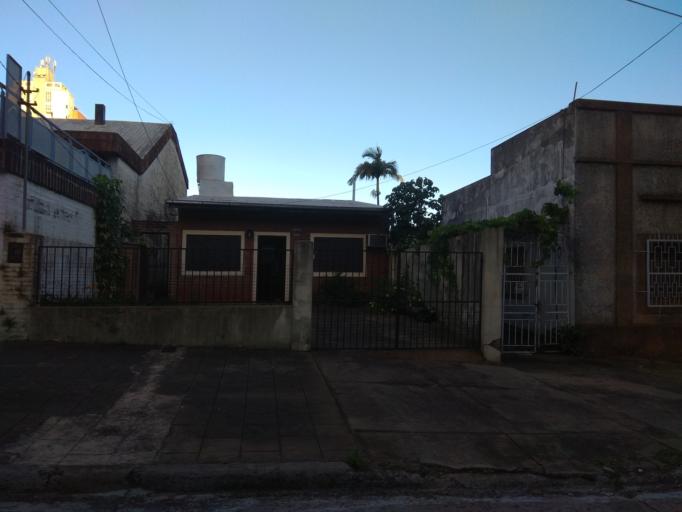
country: AR
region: Misiones
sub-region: Departamento de Capital
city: Posadas
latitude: -27.3641
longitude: -55.8890
